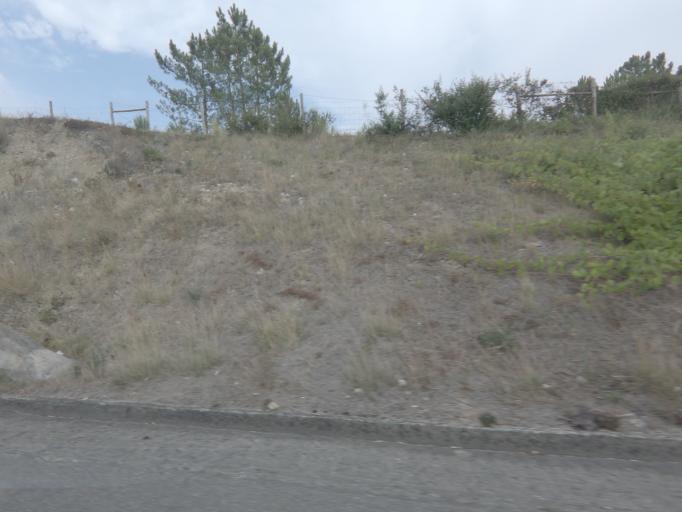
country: PT
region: Aveiro
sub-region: Mealhada
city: Pampilhosa do Botao
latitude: 40.2783
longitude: -8.4351
